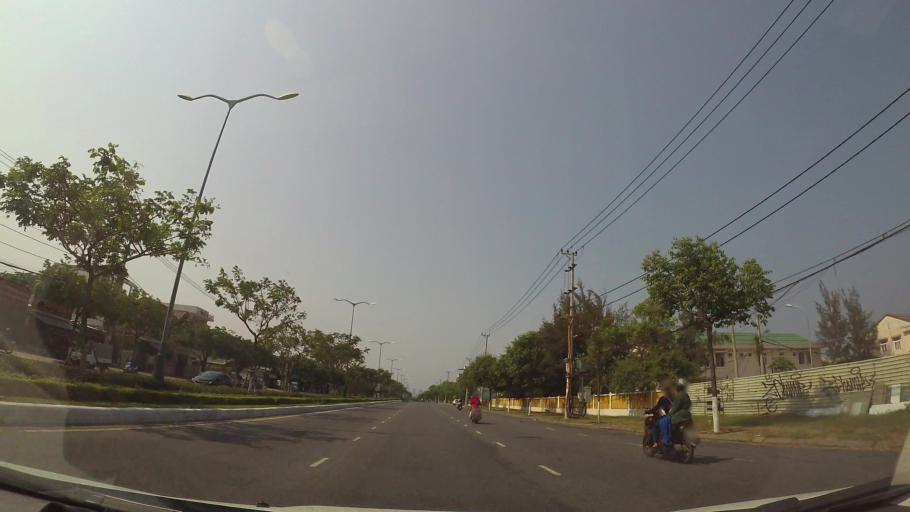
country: VN
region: Da Nang
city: Ngu Hanh Son
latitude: 16.0284
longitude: 108.2482
